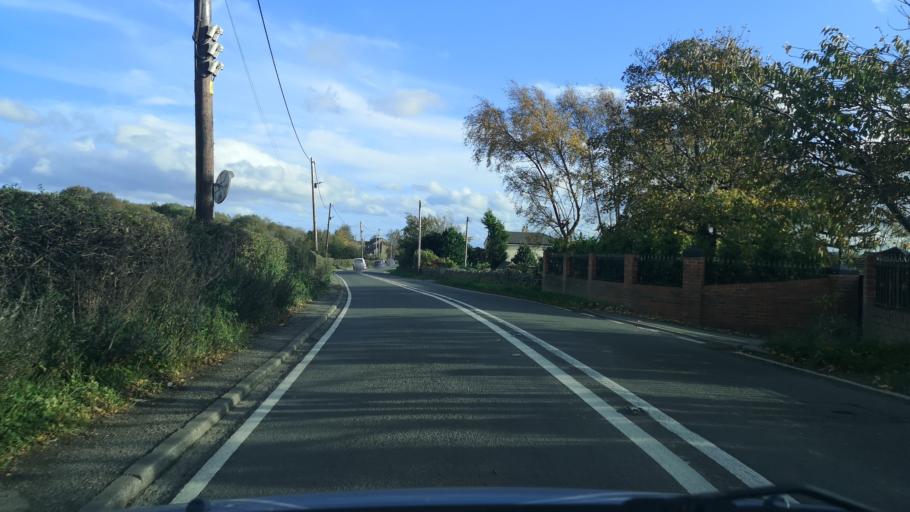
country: GB
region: England
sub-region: City and Borough of Wakefield
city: Middlestown
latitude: 53.6321
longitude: -1.6210
